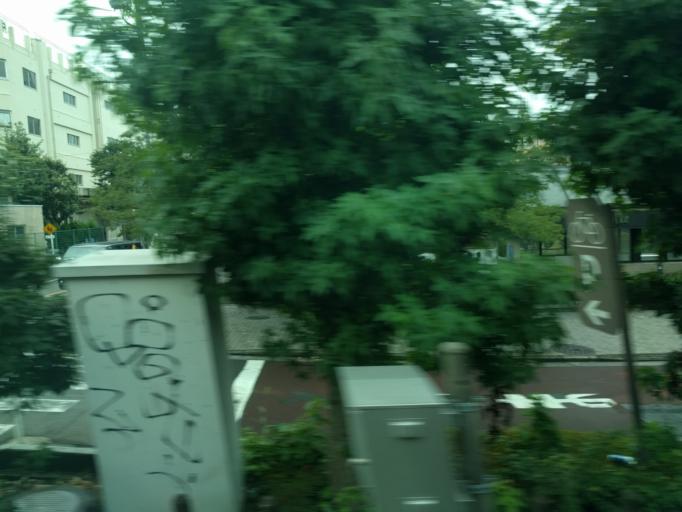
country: JP
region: Kanagawa
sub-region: Kawasaki-shi
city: Kawasaki
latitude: 35.5616
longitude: 139.7114
